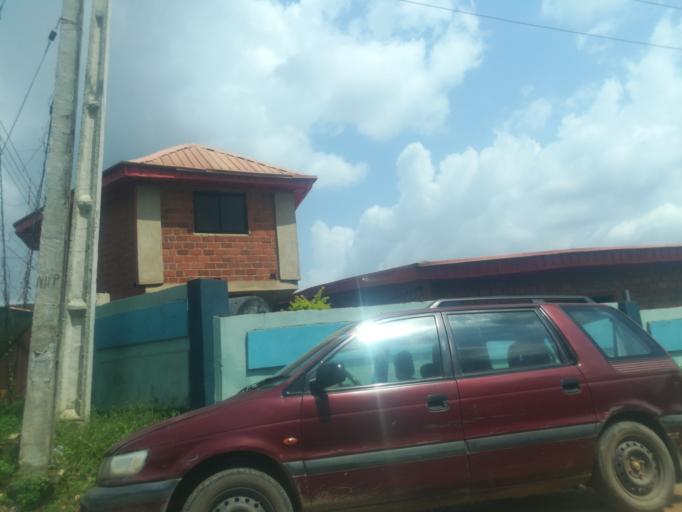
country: NG
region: Oyo
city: Ibadan
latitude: 7.3645
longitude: 3.8557
